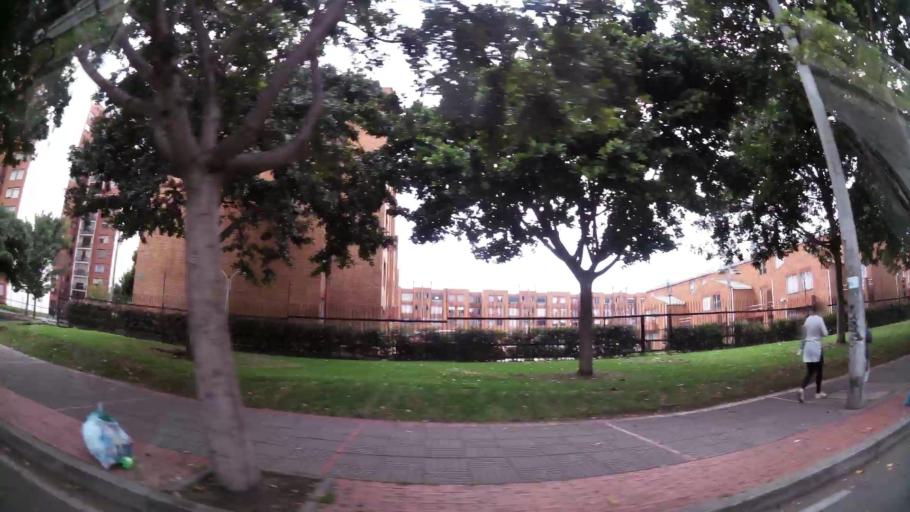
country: CO
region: Bogota D.C.
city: Barrio San Luis
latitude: 4.7359
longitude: -74.0556
